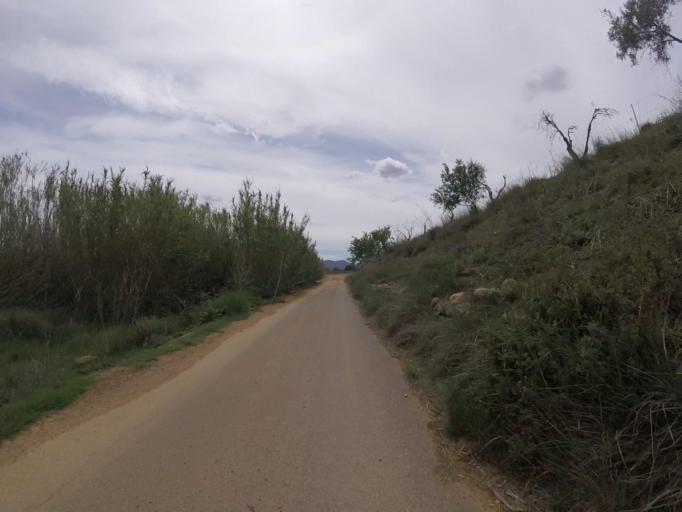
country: ES
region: Valencia
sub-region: Provincia de Castello
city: Benlloch
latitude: 40.1743
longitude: -0.0051
